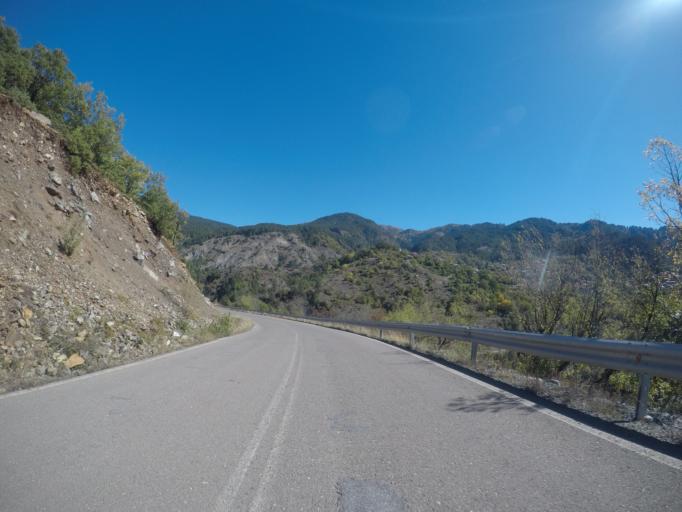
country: GR
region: Epirus
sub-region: Nomos Ioanninon
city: Konitsa
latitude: 40.0301
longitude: 21.0092
